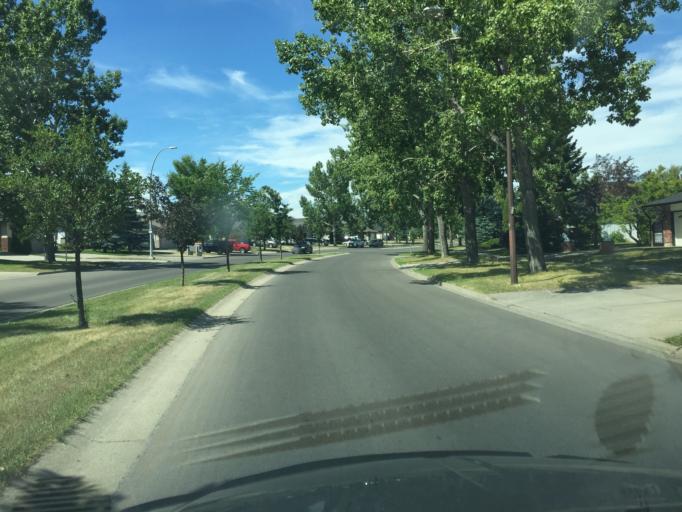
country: CA
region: Alberta
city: Calgary
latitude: 50.9334
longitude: -114.0644
